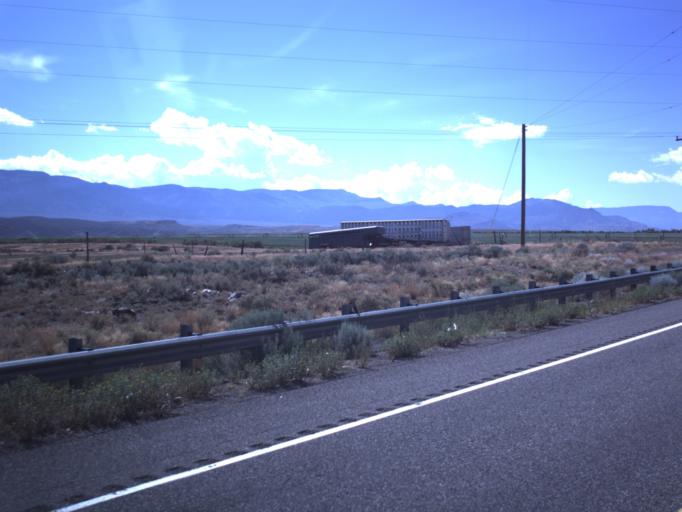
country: US
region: Utah
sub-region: Piute County
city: Junction
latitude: 38.4302
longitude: -112.2317
